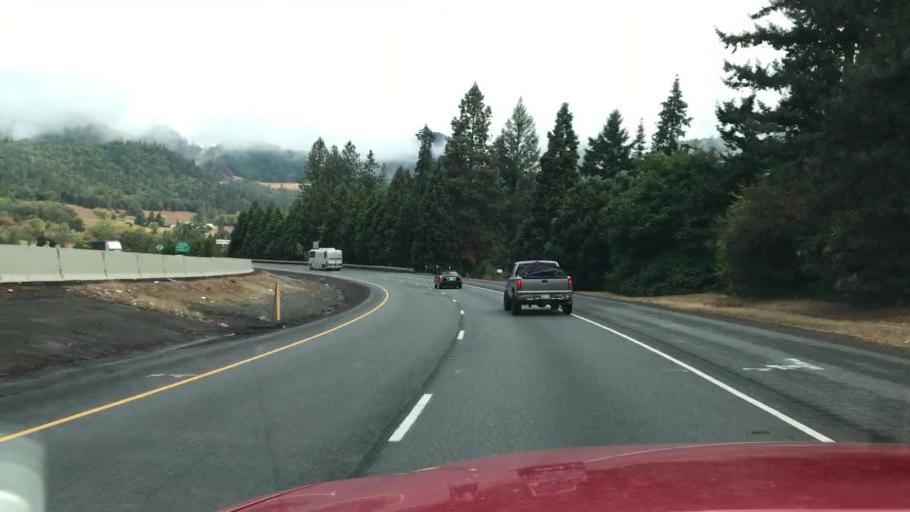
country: US
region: Oregon
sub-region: Josephine County
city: Merlin
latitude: 42.6286
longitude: -123.3804
